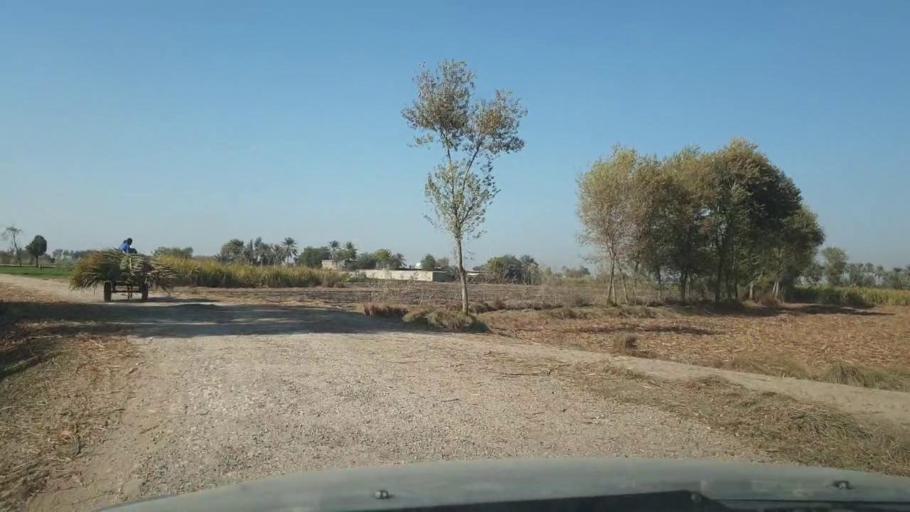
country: PK
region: Sindh
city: Ghotki
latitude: 28.0414
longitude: 69.3376
